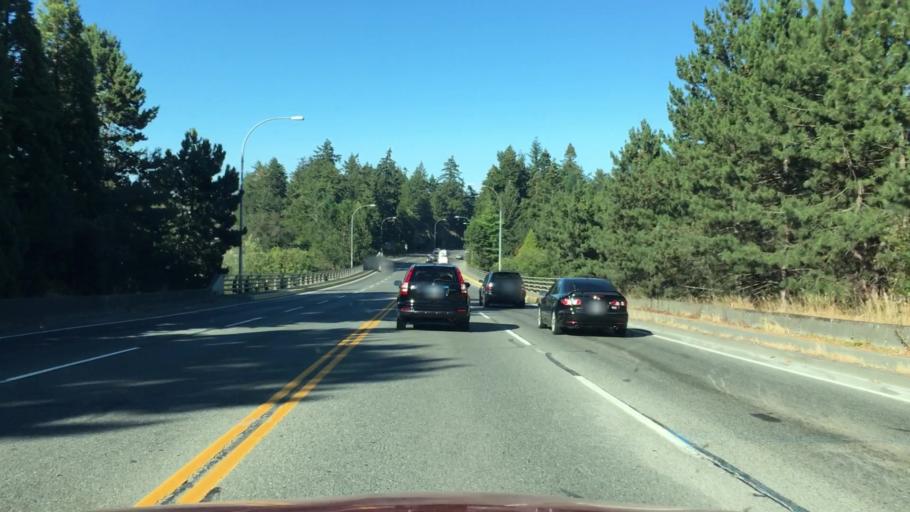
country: CA
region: British Columbia
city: Victoria
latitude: 48.4641
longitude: -123.3999
